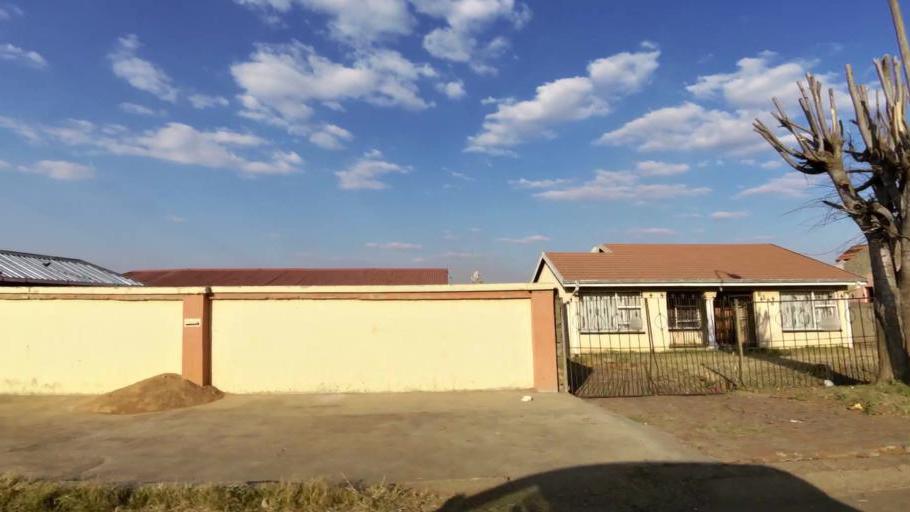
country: ZA
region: Gauteng
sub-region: City of Johannesburg Metropolitan Municipality
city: Soweto
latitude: -26.2287
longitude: 27.9051
